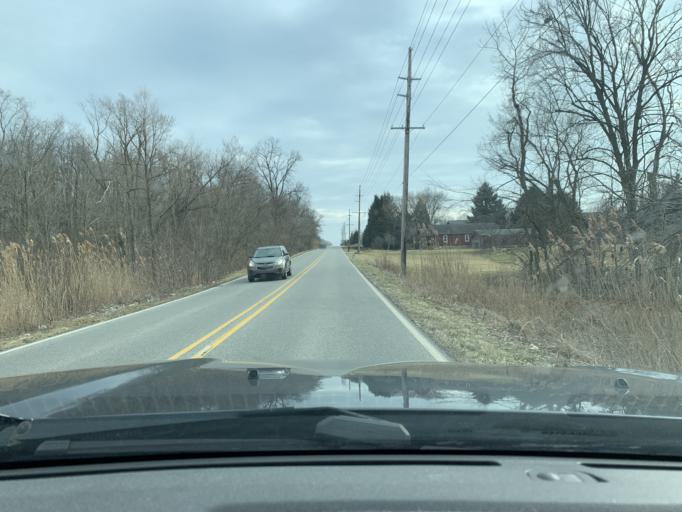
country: US
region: Indiana
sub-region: Porter County
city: Chesterton
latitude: 41.5540
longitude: -87.0664
